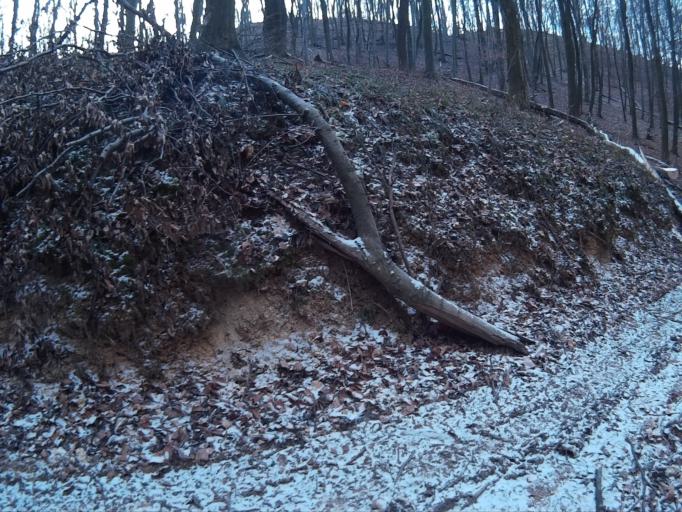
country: HU
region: Fejer
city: Szarliget
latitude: 47.5134
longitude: 18.4211
